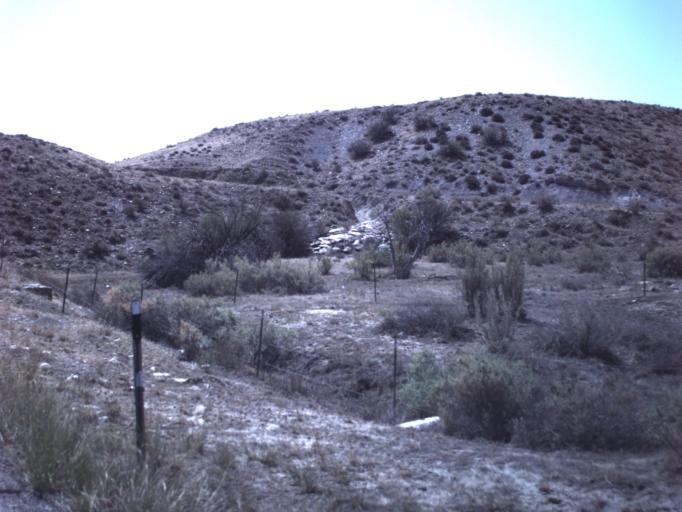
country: US
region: Utah
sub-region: Grand County
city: Moab
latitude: 38.8514
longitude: -109.2853
